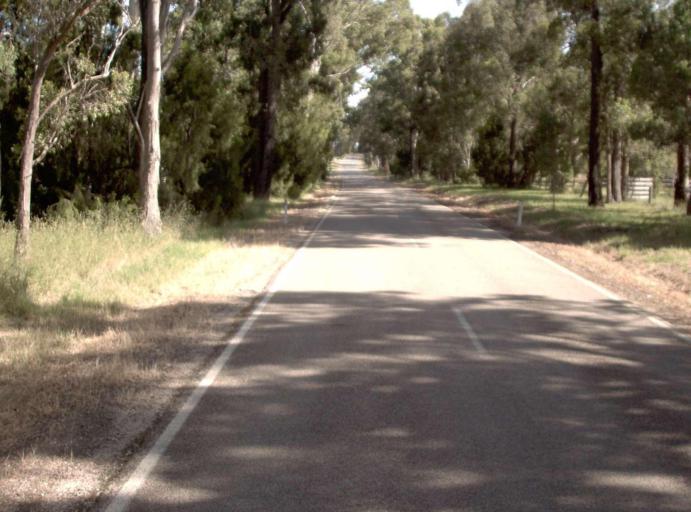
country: AU
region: Victoria
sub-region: East Gippsland
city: Lakes Entrance
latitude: -37.7703
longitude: 147.8131
